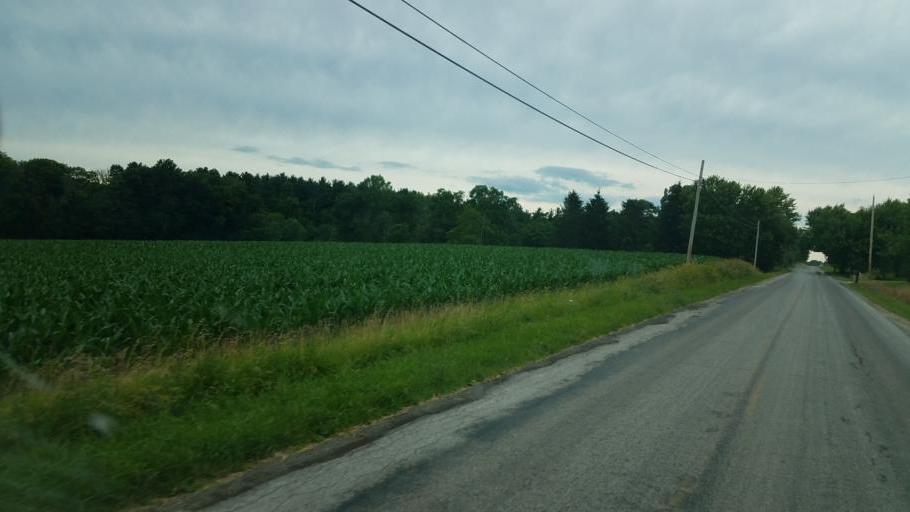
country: US
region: Ohio
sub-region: Huron County
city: Greenwich
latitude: 40.9199
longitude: -82.4423
